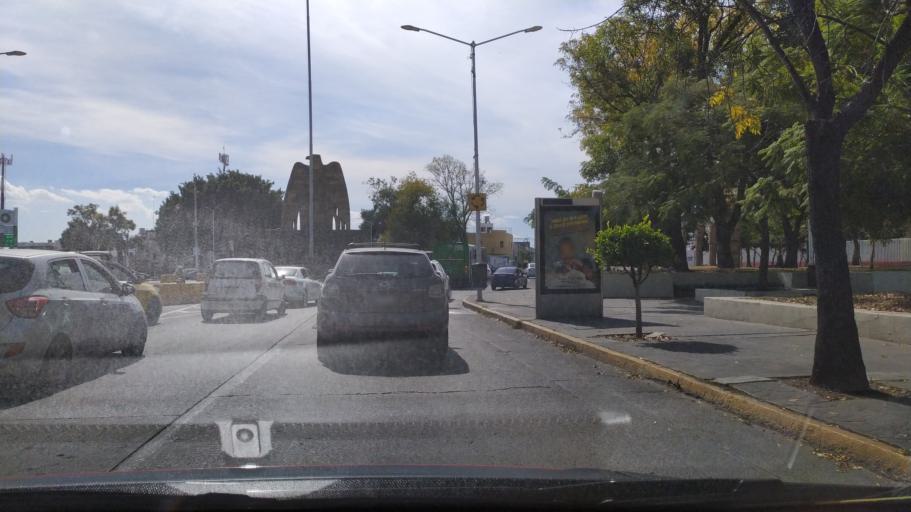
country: MX
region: Jalisco
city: Tlaquepaque
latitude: 20.6642
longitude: -103.3334
